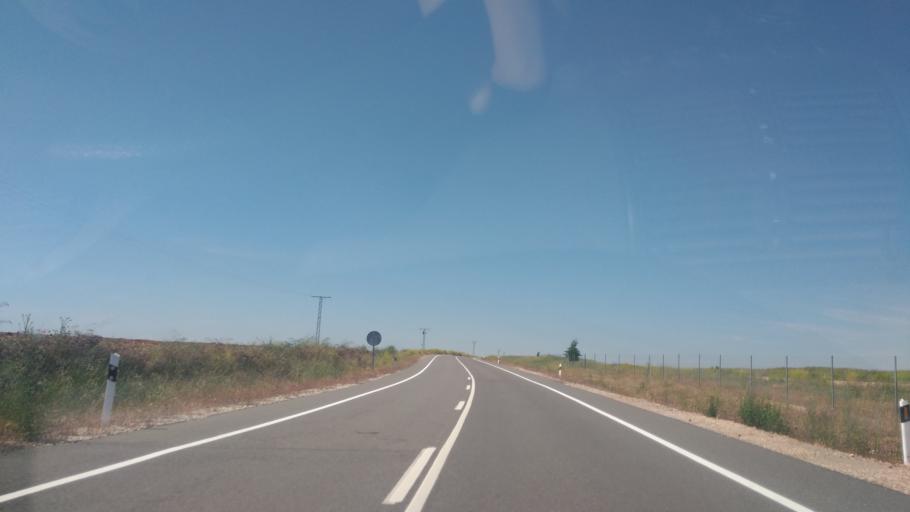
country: ES
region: Castille and Leon
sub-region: Provincia de Salamanca
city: Calzada de Valdunciel
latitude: 41.1050
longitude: -5.6992
